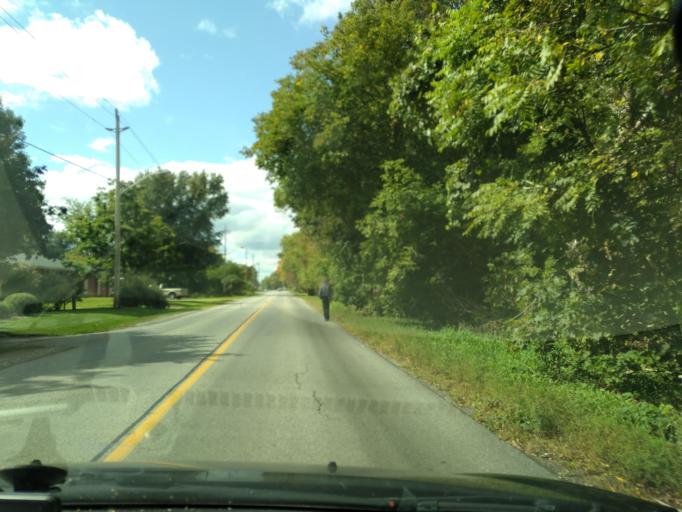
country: CA
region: Ontario
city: Newmarket
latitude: 44.1060
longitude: -79.5110
